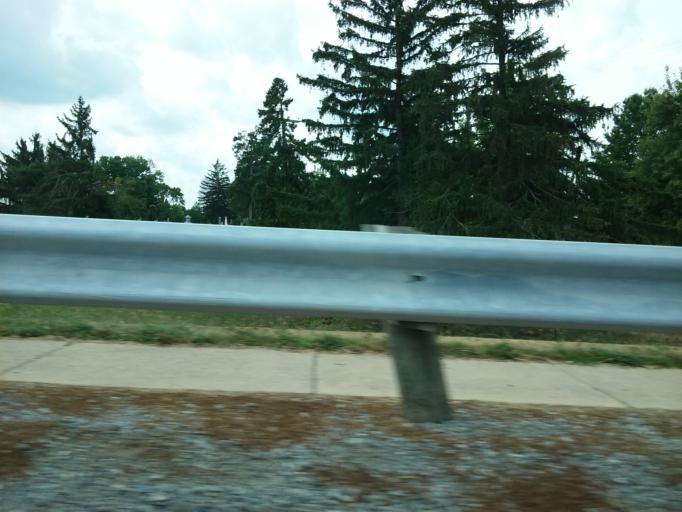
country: US
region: Ohio
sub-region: Hancock County
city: Findlay
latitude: 41.0465
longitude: -83.6636
